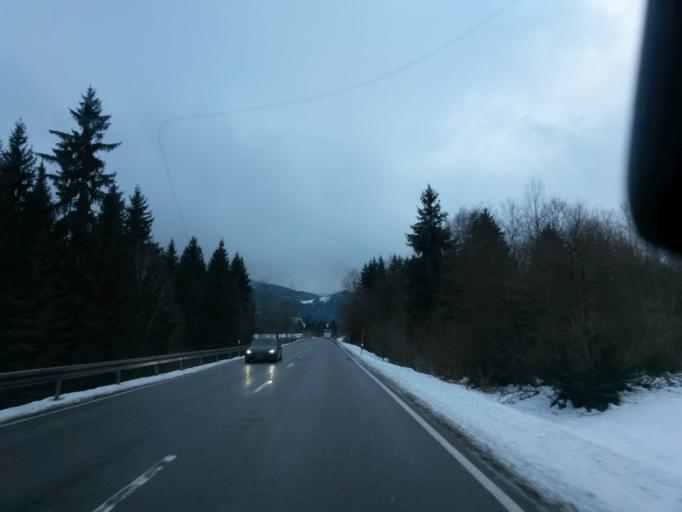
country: DE
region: Bavaria
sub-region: Swabia
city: Oy-Mittelberg
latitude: 47.6147
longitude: 10.4342
